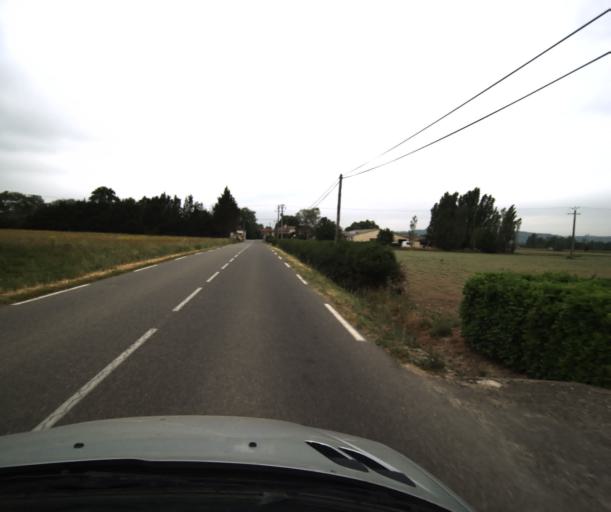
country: FR
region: Midi-Pyrenees
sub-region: Departement du Tarn-et-Garonne
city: Saint-Nicolas-de-la-Grave
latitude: 44.0692
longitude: 1.0096
